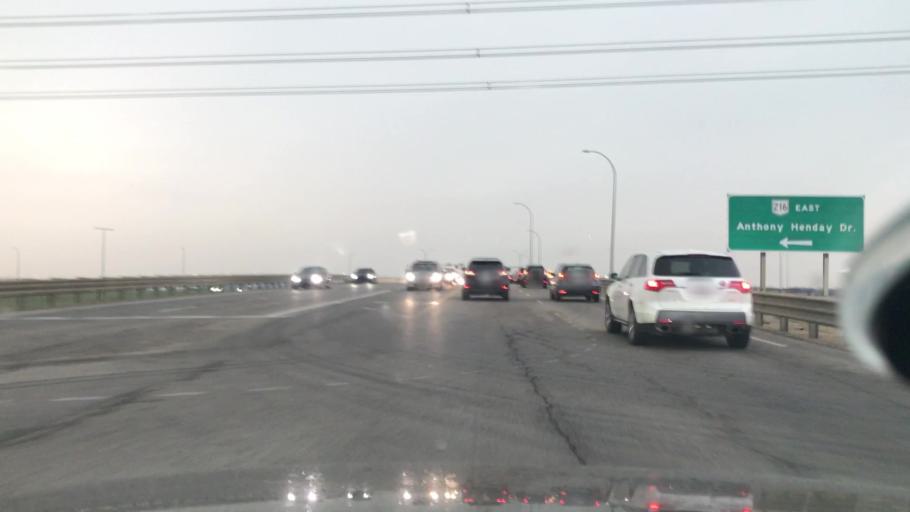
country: CA
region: Alberta
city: Devon
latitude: 53.4447
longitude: -113.5984
